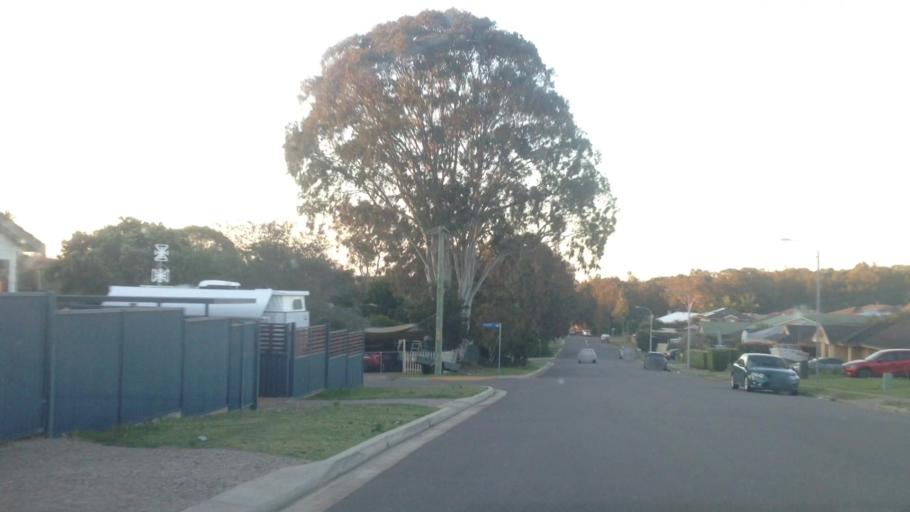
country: AU
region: New South Wales
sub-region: Wyong Shire
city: Kingfisher Shores
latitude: -33.1447
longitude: 151.5203
